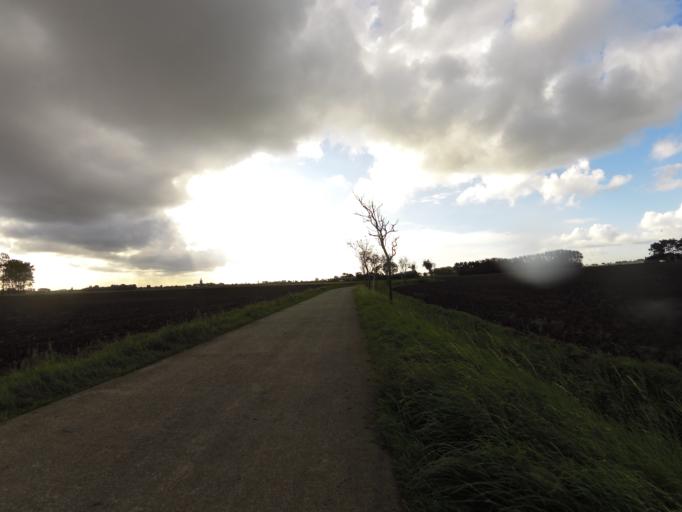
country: BE
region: Flanders
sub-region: Provincie West-Vlaanderen
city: Middelkerke
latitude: 51.1847
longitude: 2.8567
